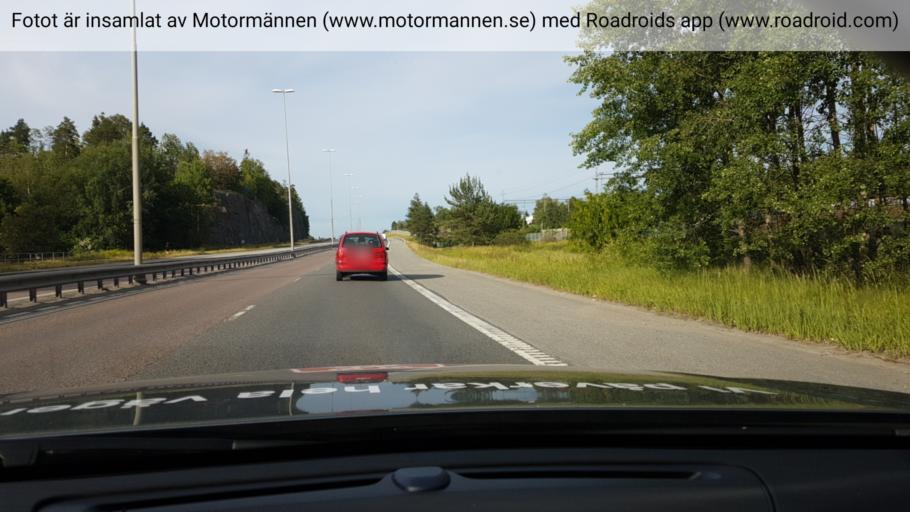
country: SE
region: Stockholm
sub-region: Huddinge Kommun
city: Huddinge
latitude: 59.2270
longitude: 17.9586
